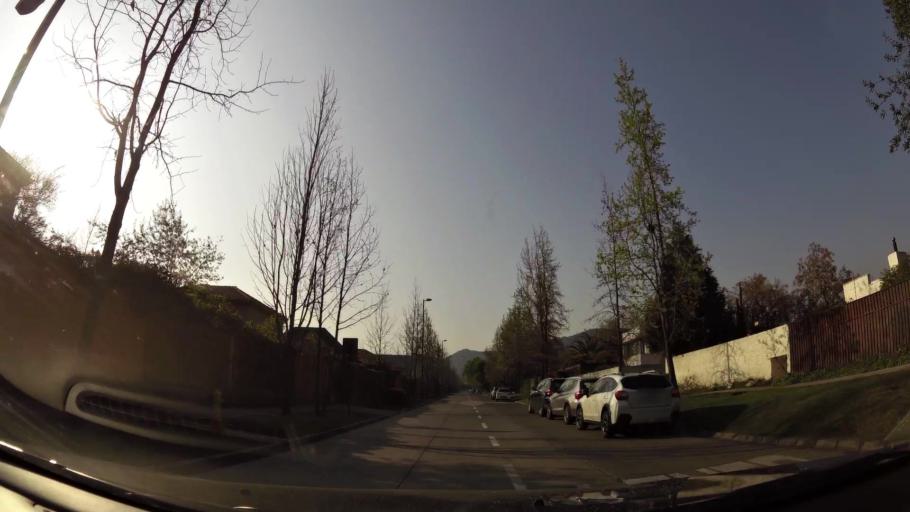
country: CL
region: Santiago Metropolitan
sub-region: Provincia de Santiago
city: Villa Presidente Frei, Nunoa, Santiago, Chile
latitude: -33.3589
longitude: -70.5339
